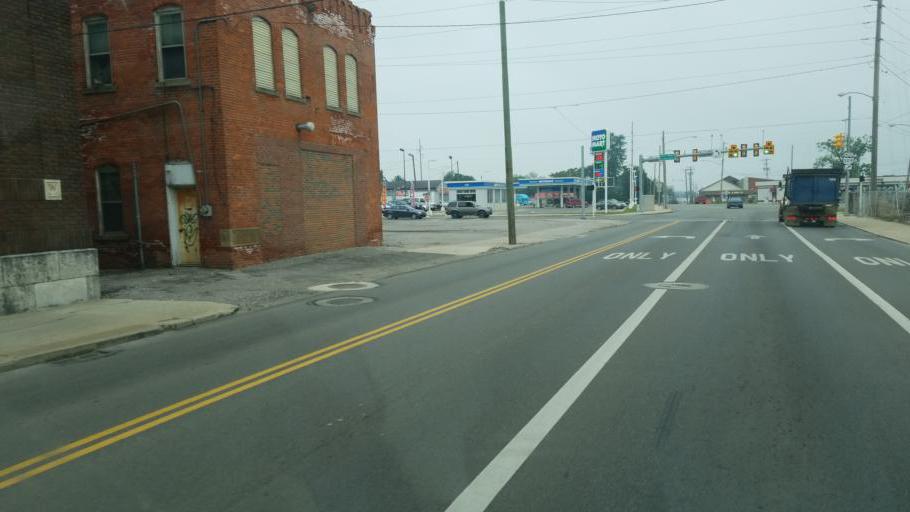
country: US
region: Ohio
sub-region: Marion County
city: Marion
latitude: 40.5887
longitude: -83.1425
